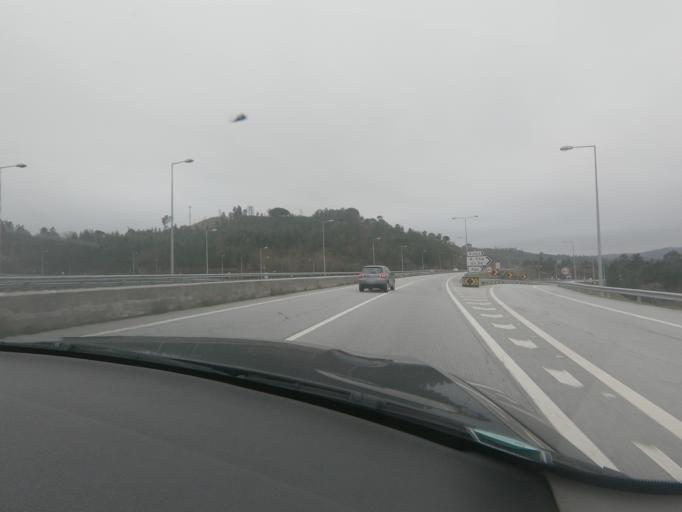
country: PT
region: Viseu
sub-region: Viseu
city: Viseu
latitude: 40.6143
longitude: -7.9640
